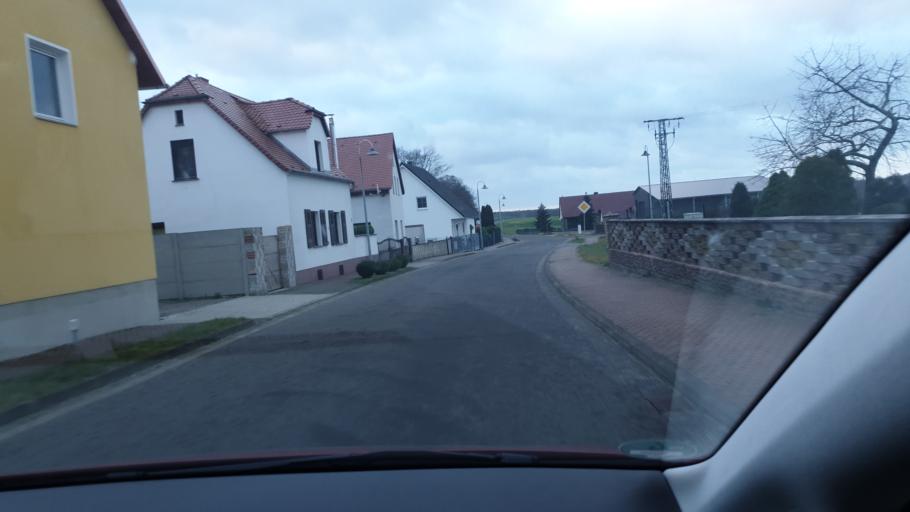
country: DE
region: Saxony
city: Falkenhain
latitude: 51.4522
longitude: 12.8659
